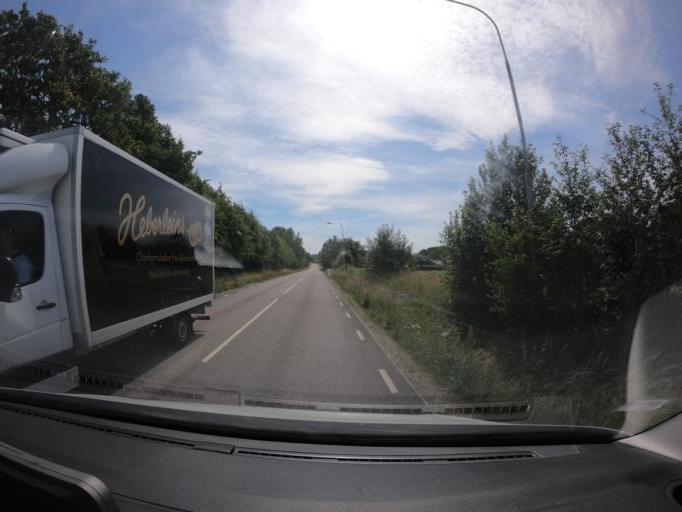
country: SE
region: Skane
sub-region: Bastads Kommun
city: Forslov
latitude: 56.4155
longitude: 12.7392
